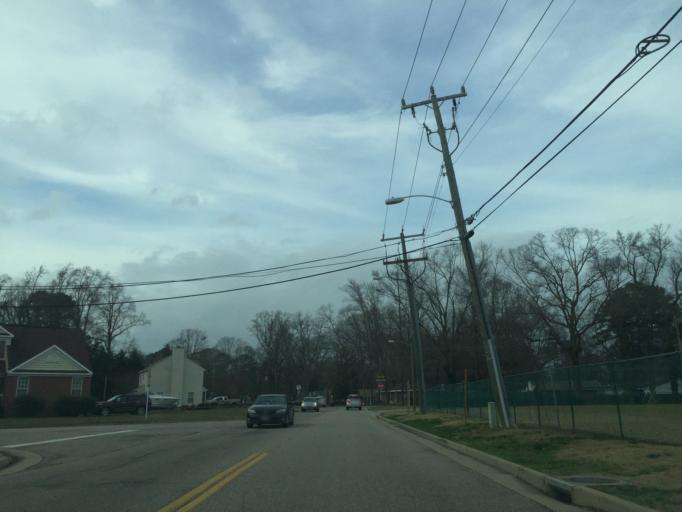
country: US
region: Virginia
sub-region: City of Newport News
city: Newport News
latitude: 37.0641
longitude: -76.5015
